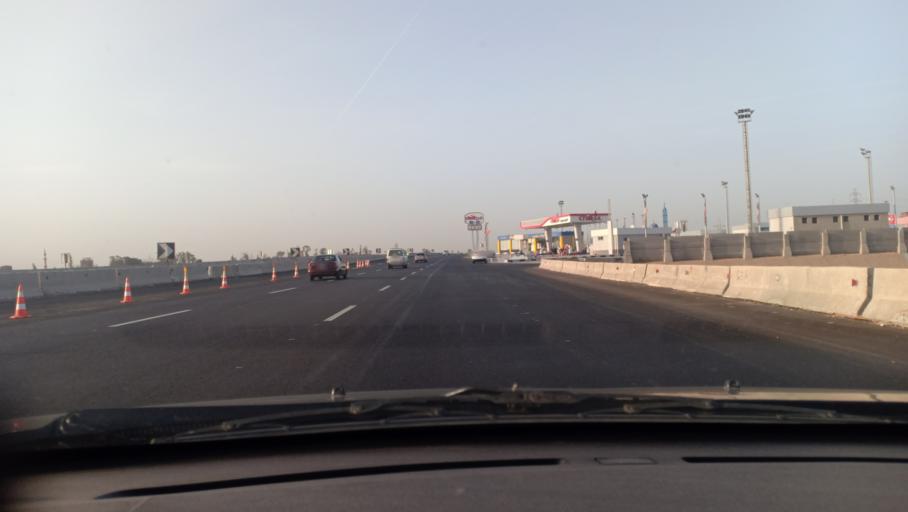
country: EG
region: Muhafazat al Qalyubiyah
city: Toukh
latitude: 30.3036
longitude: 31.2199
